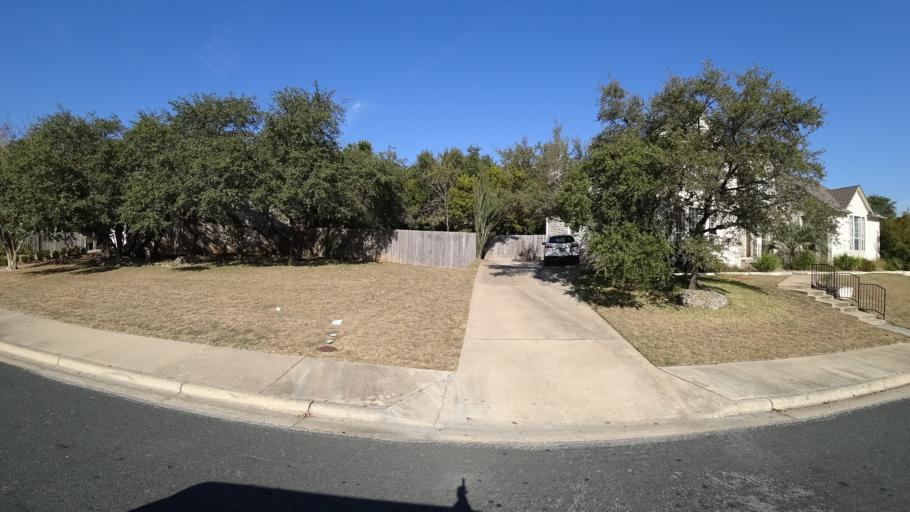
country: US
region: Texas
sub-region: Williamson County
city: Jollyville
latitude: 30.3956
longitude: -97.7715
